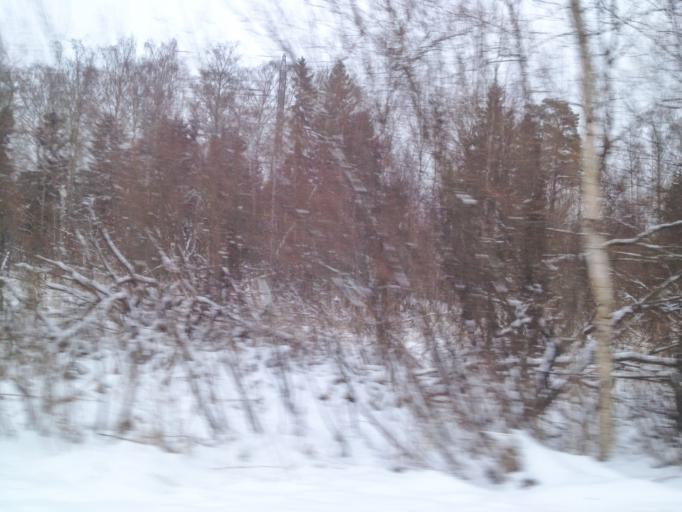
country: FI
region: Uusimaa
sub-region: Helsinki
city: Vantaa
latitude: 60.2191
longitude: 25.1580
